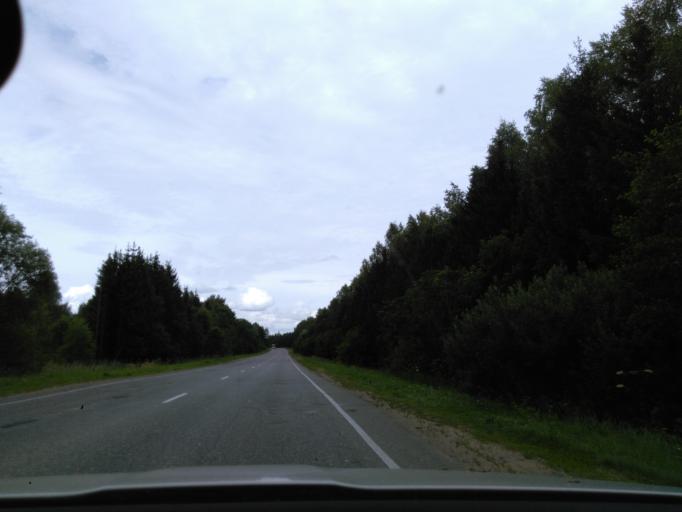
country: RU
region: Tverskaya
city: Konakovo
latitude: 56.6587
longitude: 36.7157
